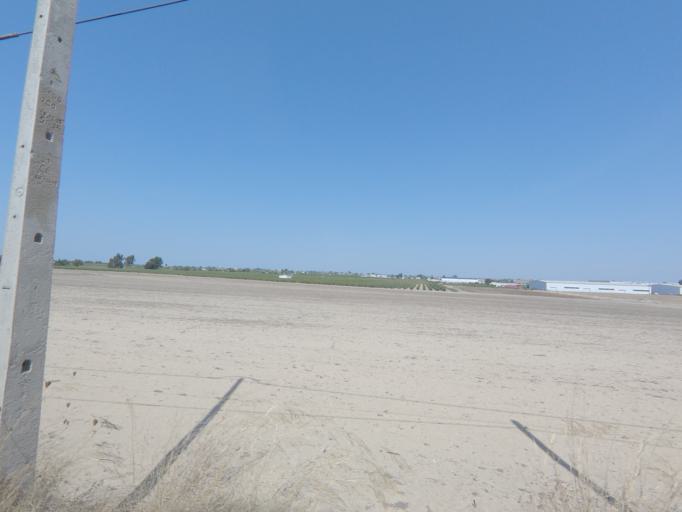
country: PT
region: Setubal
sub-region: Palmela
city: Palmela
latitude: 38.5904
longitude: -8.8527
